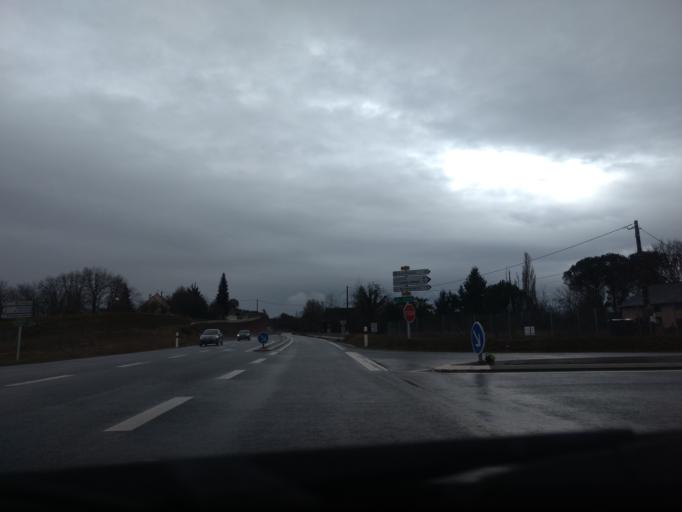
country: FR
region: Midi-Pyrenees
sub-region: Departement de l'Aveyron
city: Firmi
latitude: 44.5140
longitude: 2.3578
